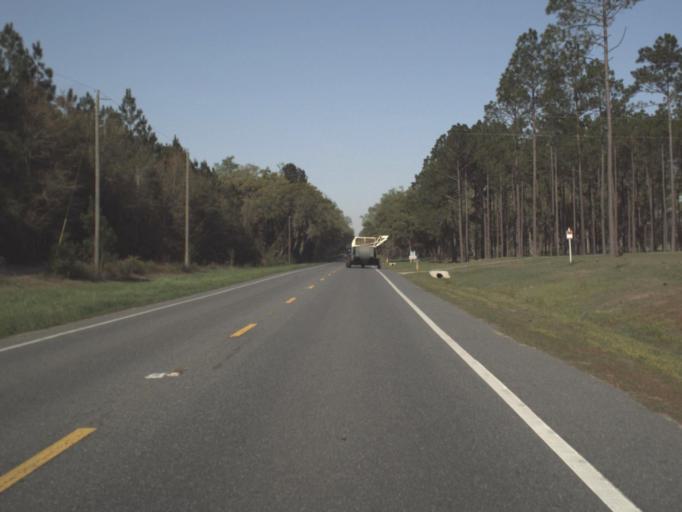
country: US
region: Florida
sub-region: Jackson County
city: Malone
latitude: 30.9589
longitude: -85.1831
